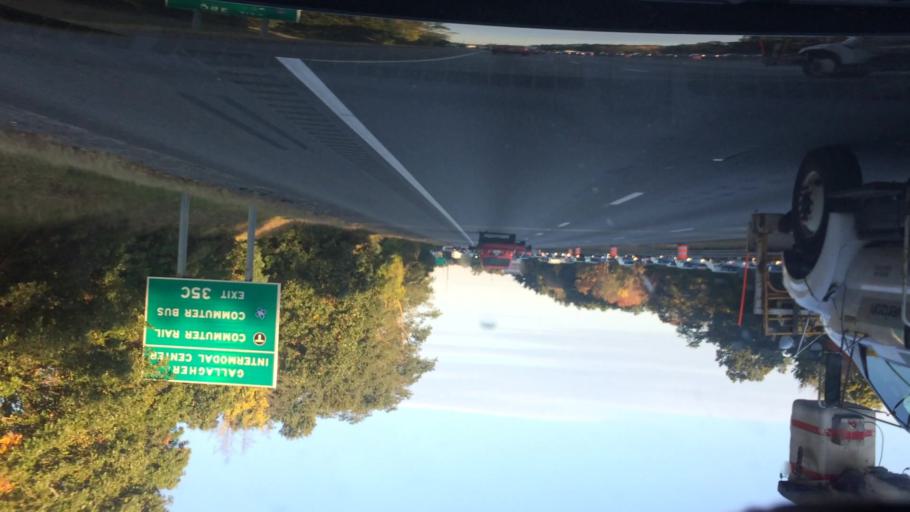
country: US
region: Massachusetts
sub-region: Middlesex County
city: Lowell
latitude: 42.6114
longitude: -71.3084
